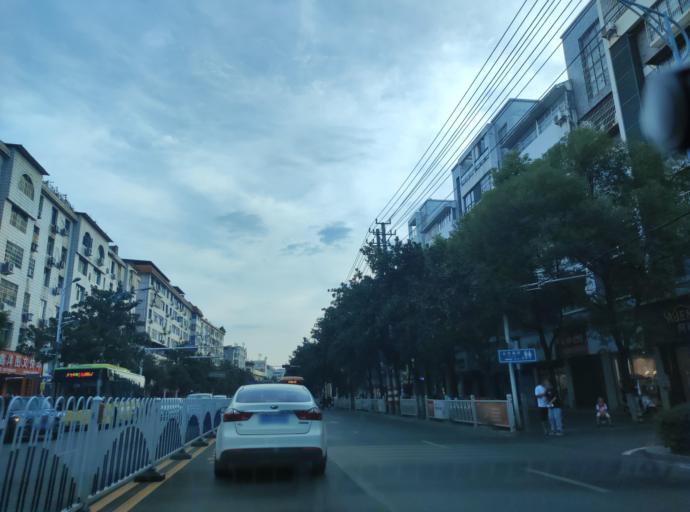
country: CN
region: Jiangxi Sheng
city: Pingxiang
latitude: 27.6336
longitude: 113.8553
